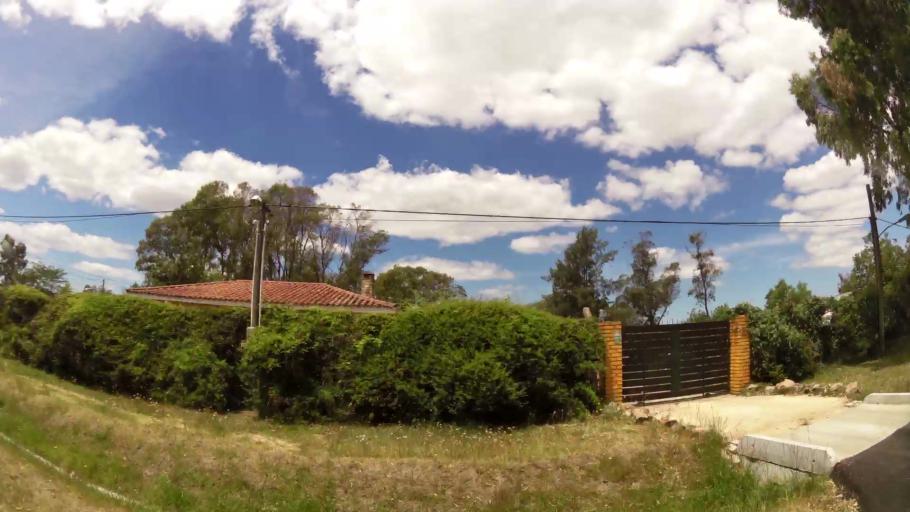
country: UY
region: Canelones
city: Colonia Nicolich
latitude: -34.8253
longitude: -55.9685
